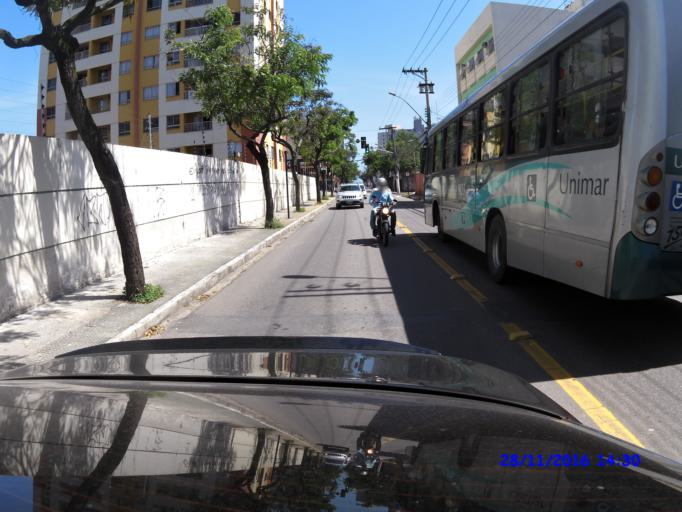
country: BR
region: Espirito Santo
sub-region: Vila Velha
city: Vila Velha
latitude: -20.2606
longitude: -40.2637
